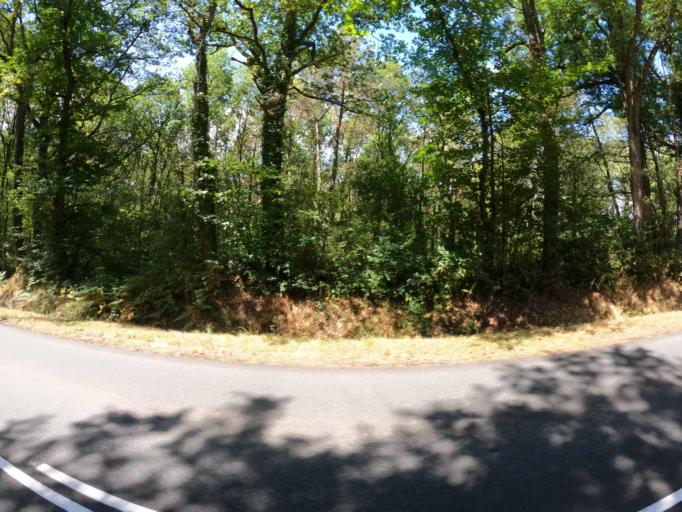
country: FR
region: Pays de la Loire
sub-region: Departement de Maine-et-Loire
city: Champigne
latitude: 47.6226
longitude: -0.5828
